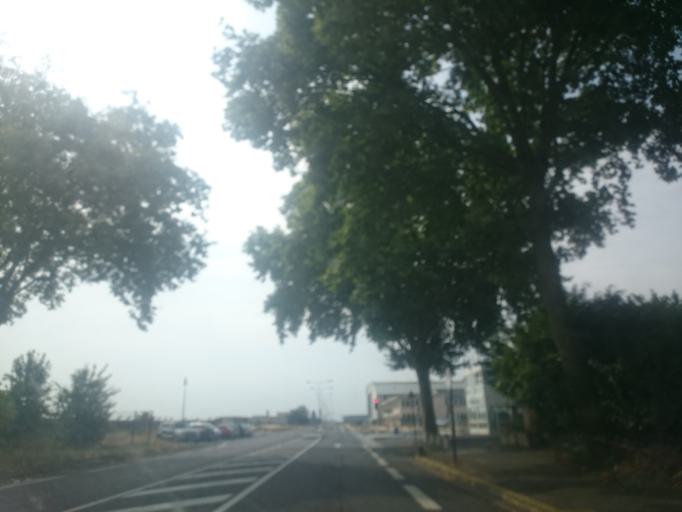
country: FR
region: Ile-de-France
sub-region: Departement du Val-de-Marne
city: Rungis
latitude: 48.7444
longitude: 2.3693
